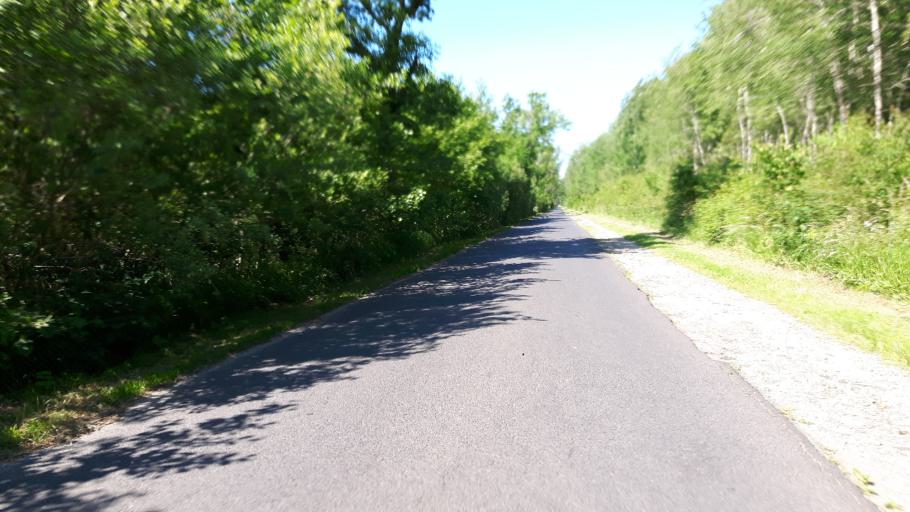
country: PL
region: Pomeranian Voivodeship
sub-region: Powiat slupski
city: Glowczyce
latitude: 54.6544
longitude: 17.4205
